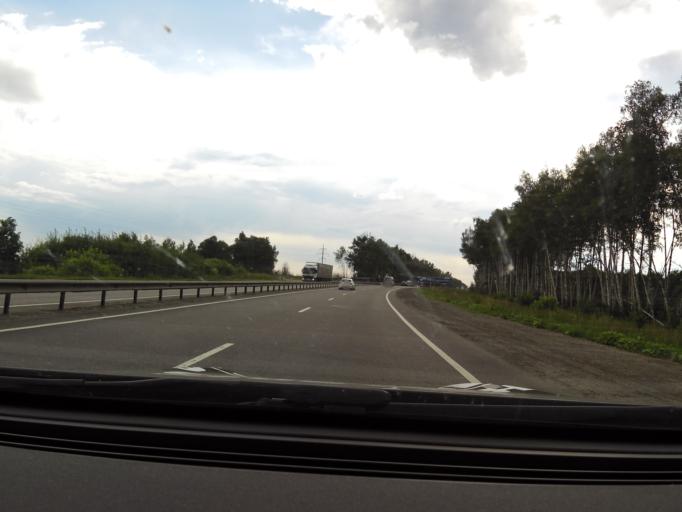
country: RU
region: Vladimir
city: Gorokhovets
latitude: 56.1614
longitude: 42.6050
